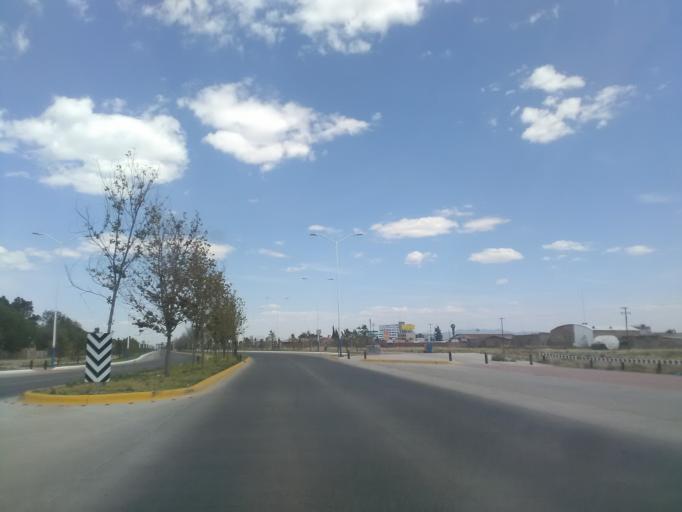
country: MX
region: Durango
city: Victoria de Durango
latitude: 24.0365
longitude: -104.6702
